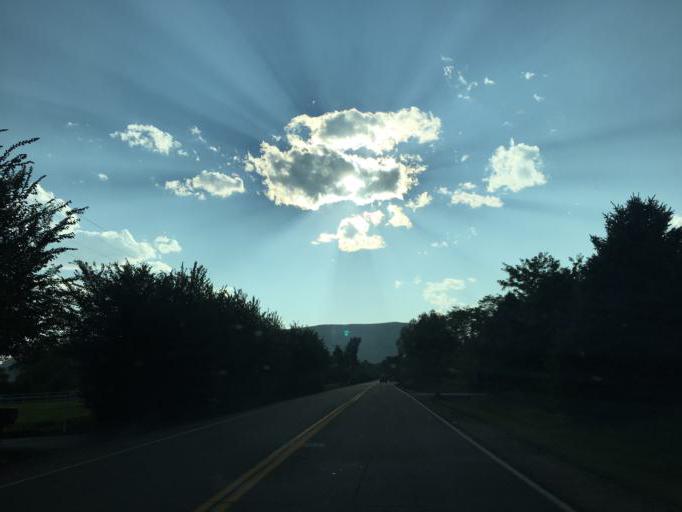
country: US
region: Colorado
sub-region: Jefferson County
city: Applewood
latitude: 39.7907
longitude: -105.1667
